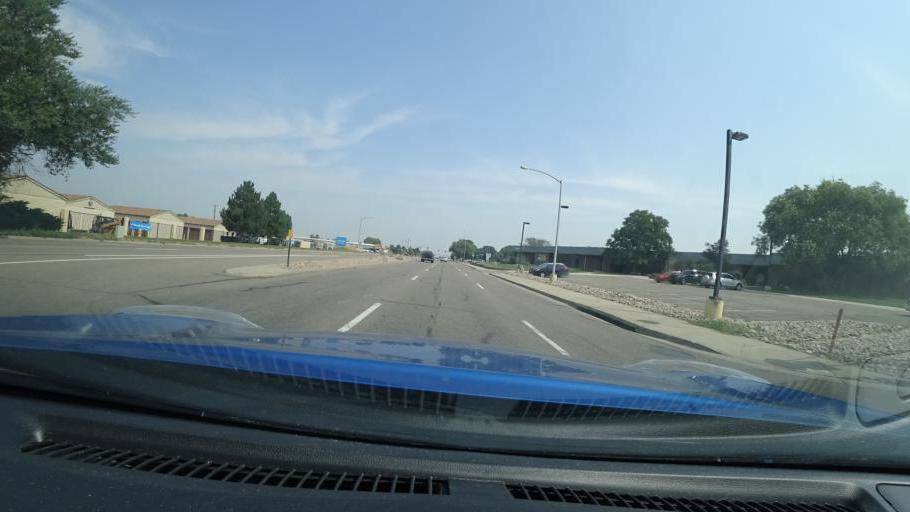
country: US
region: Colorado
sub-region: Adams County
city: Aurora
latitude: 39.7217
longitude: -104.7911
